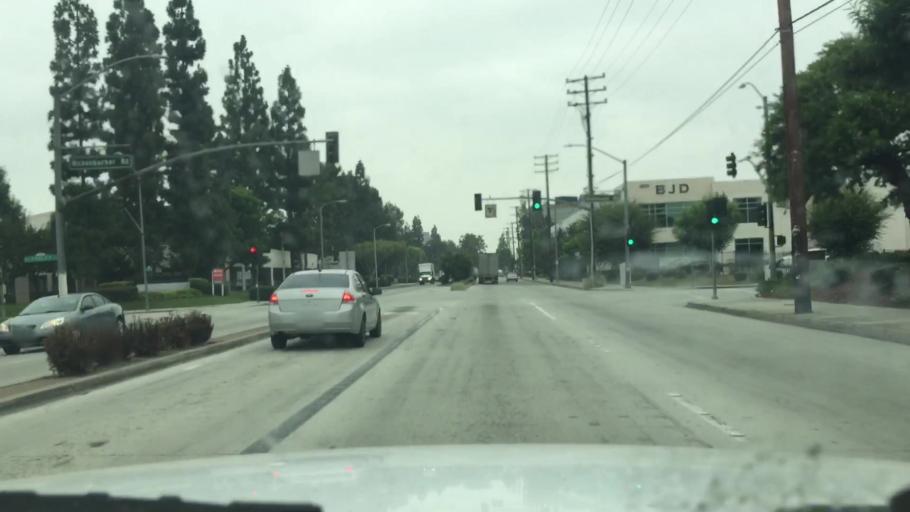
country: US
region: California
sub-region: Los Angeles County
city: Commerce
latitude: 33.9895
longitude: -118.1616
